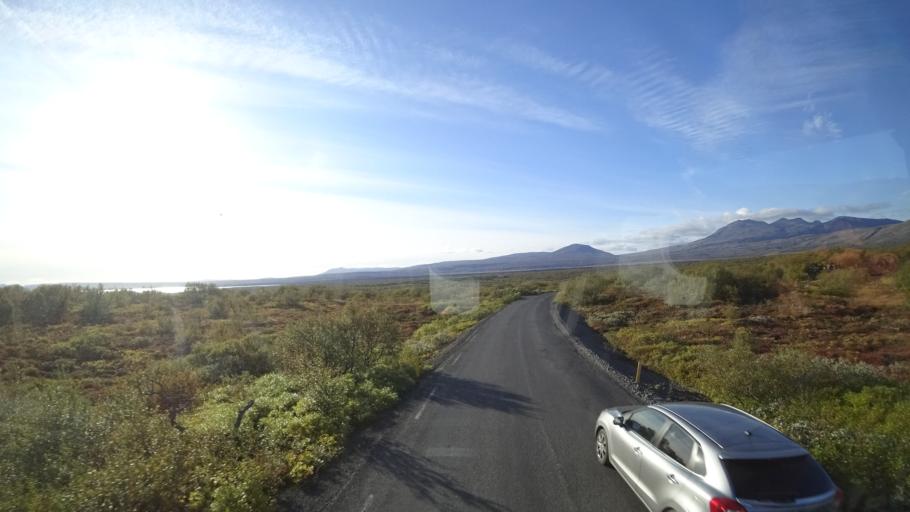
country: IS
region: South
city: Hveragerdi
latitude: 64.2582
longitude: -21.0344
